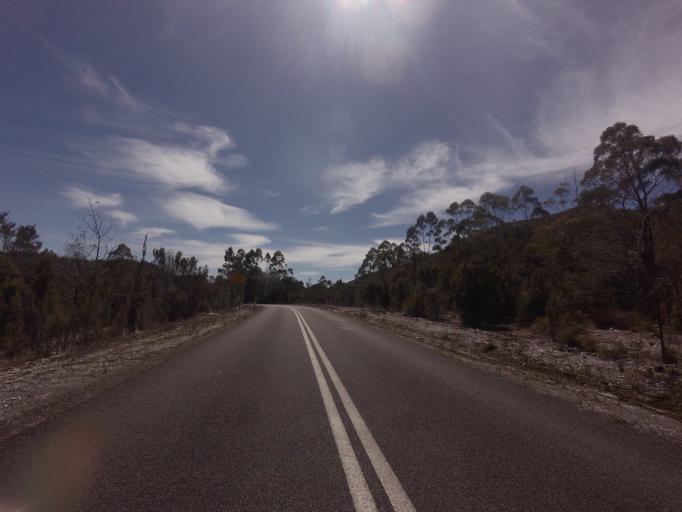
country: AU
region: Tasmania
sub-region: West Coast
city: Queenstown
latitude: -42.7681
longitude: 146.0561
